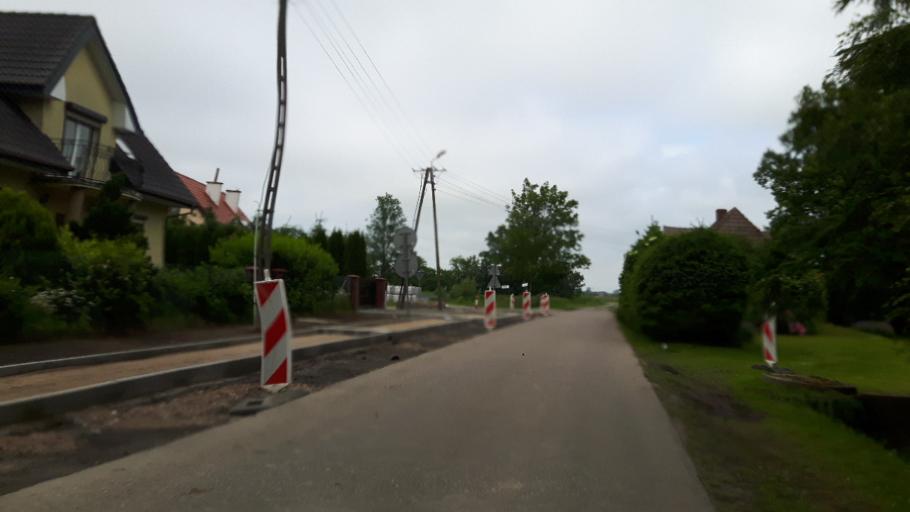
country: PL
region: West Pomeranian Voivodeship
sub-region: Powiat koszalinski
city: Sianow
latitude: 54.2993
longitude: 16.2790
